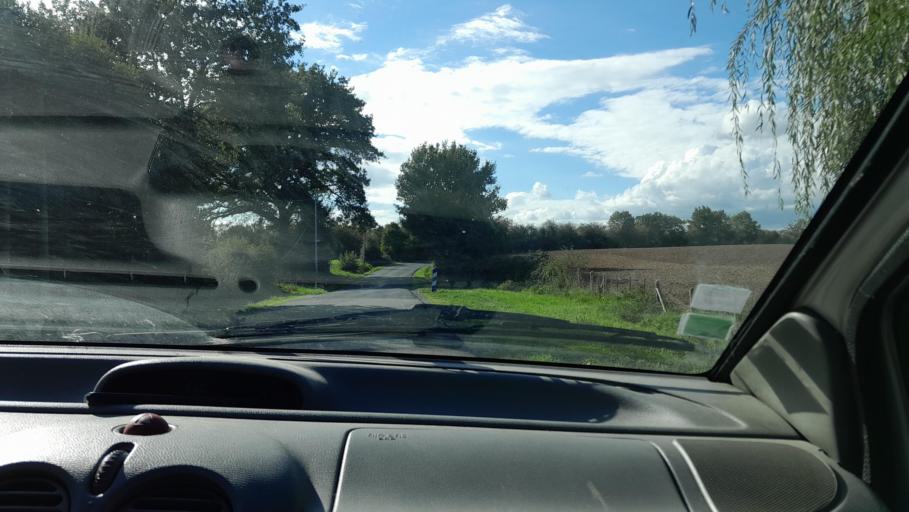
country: FR
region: Pays de la Loire
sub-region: Departement de la Mayenne
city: Ahuille
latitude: 48.0198
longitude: -0.8743
